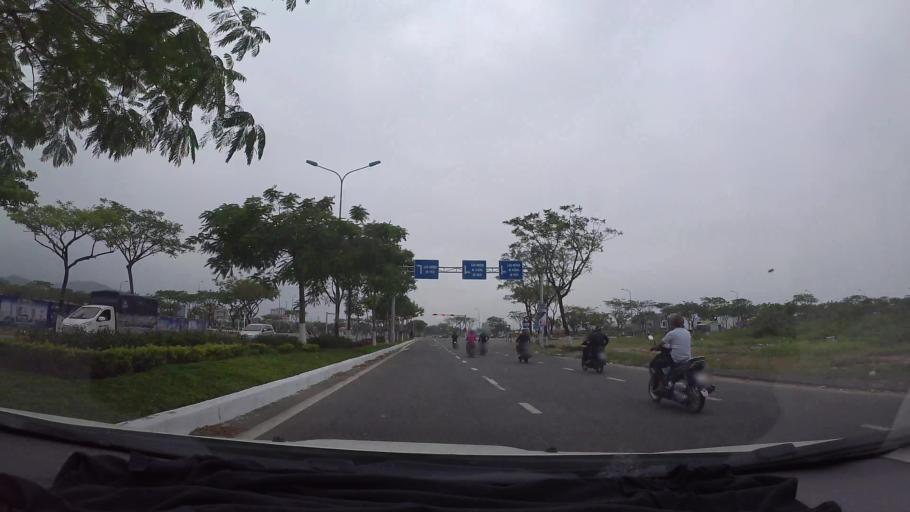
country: VN
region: Da Nang
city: Lien Chieu
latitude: 16.0730
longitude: 108.1619
